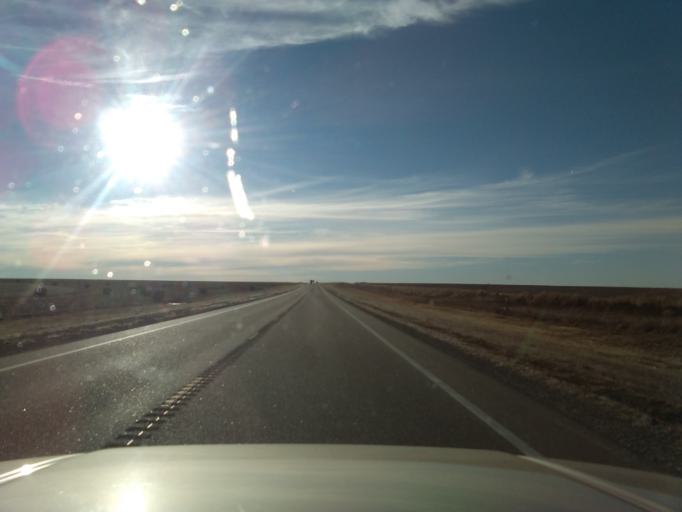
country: US
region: Kansas
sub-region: Sheridan County
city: Hoxie
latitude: 39.5315
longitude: -100.5971
